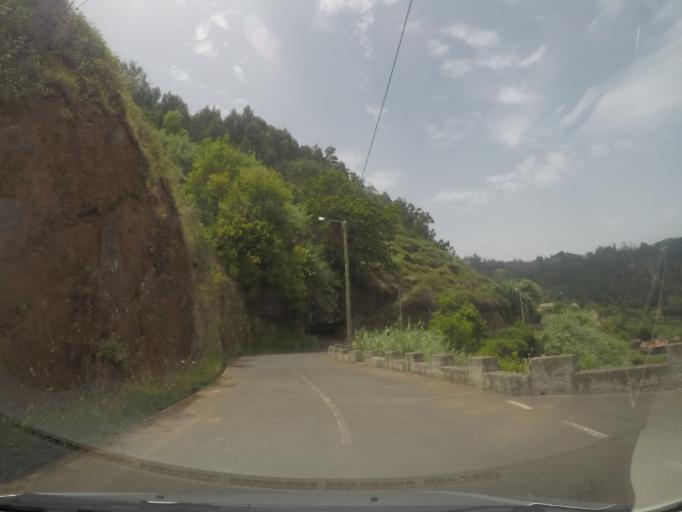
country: PT
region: Madeira
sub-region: Santa Cruz
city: Camacha
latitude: 32.6772
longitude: -16.8376
